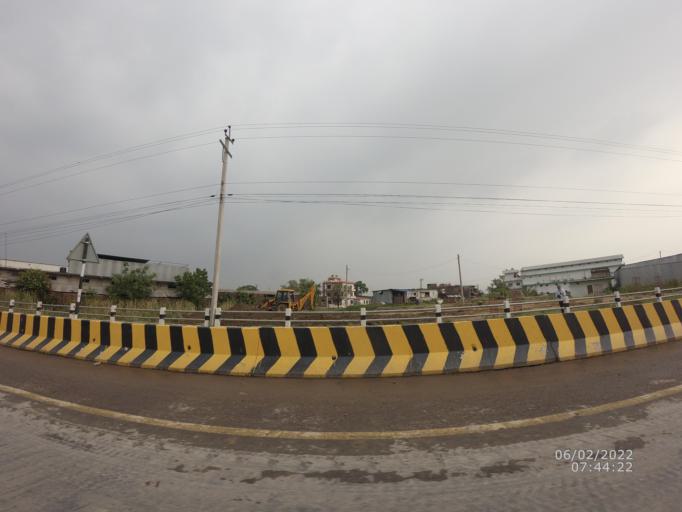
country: NP
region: Western Region
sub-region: Lumbini Zone
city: Bhairahawa
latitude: 27.5158
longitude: 83.4362
